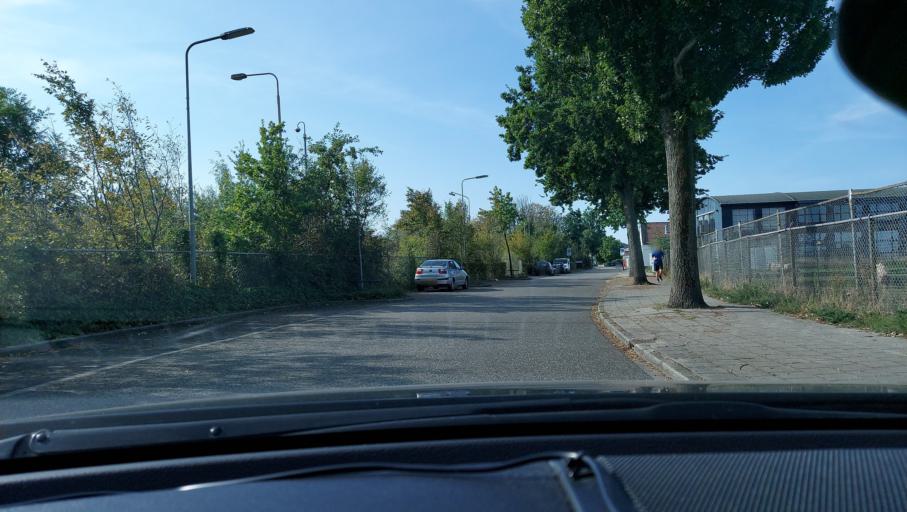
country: NL
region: Limburg
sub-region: Gemeente Roermond
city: Leeuwen
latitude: 51.1989
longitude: 6.0012
